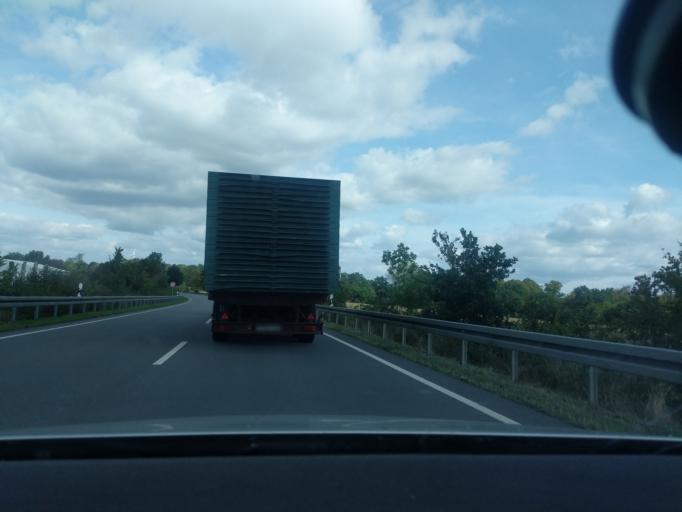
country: DE
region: Lower Saxony
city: Bohmte
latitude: 52.3769
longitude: 8.3083
